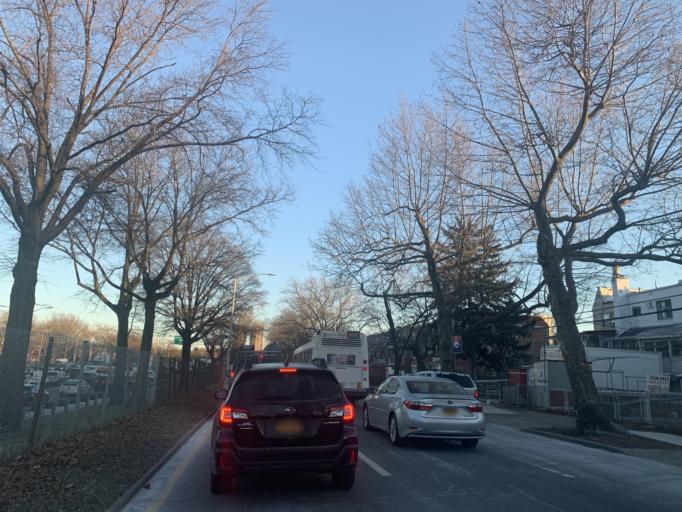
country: US
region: New York
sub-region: Queens County
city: Jamaica
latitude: 40.7403
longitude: -73.8201
